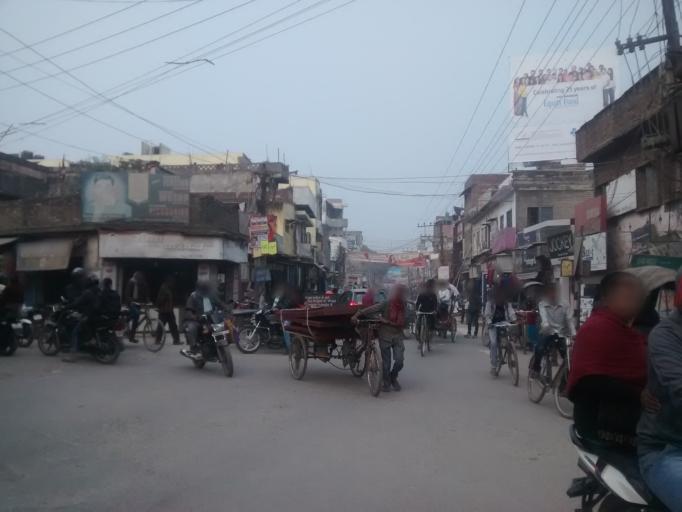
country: IN
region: Bihar
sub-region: Muzaffarpur
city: Muzaffarpur
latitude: 26.1176
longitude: 85.3925
